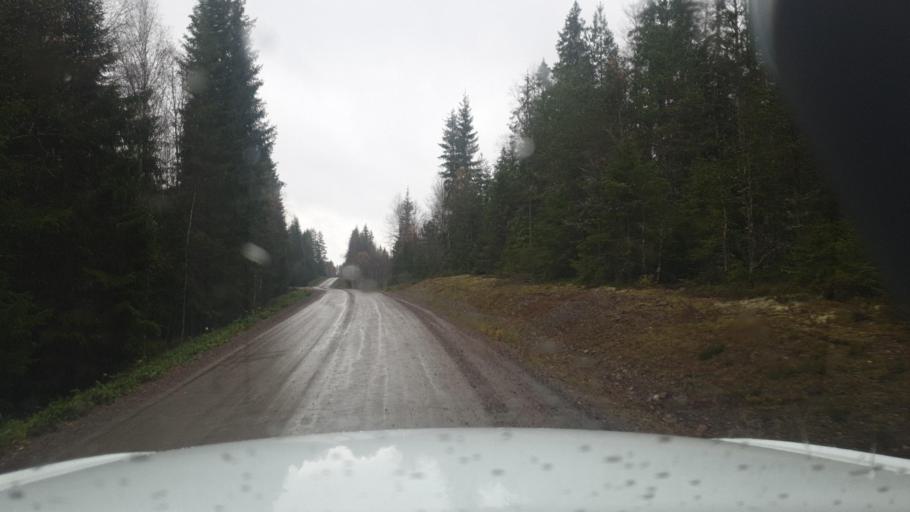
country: SE
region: Vaermland
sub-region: Eda Kommun
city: Charlottenberg
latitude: 60.0546
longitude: 12.5605
